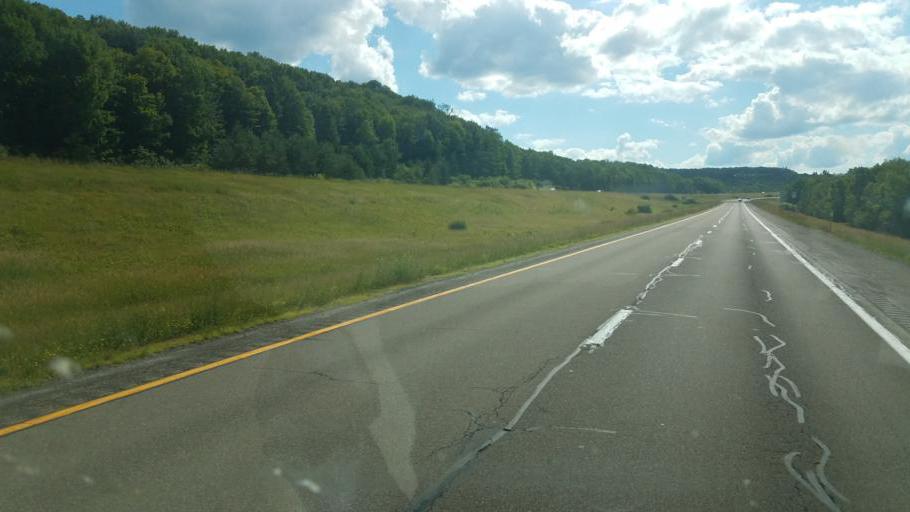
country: US
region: New York
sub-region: Allegany County
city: Alfred
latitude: 42.3182
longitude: -77.8096
